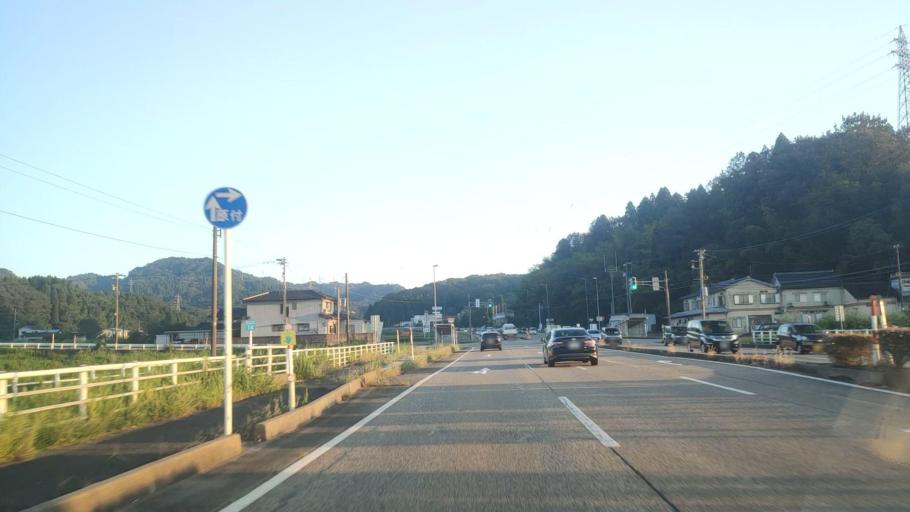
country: JP
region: Toyama
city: Himi
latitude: 36.8106
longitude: 136.9968
